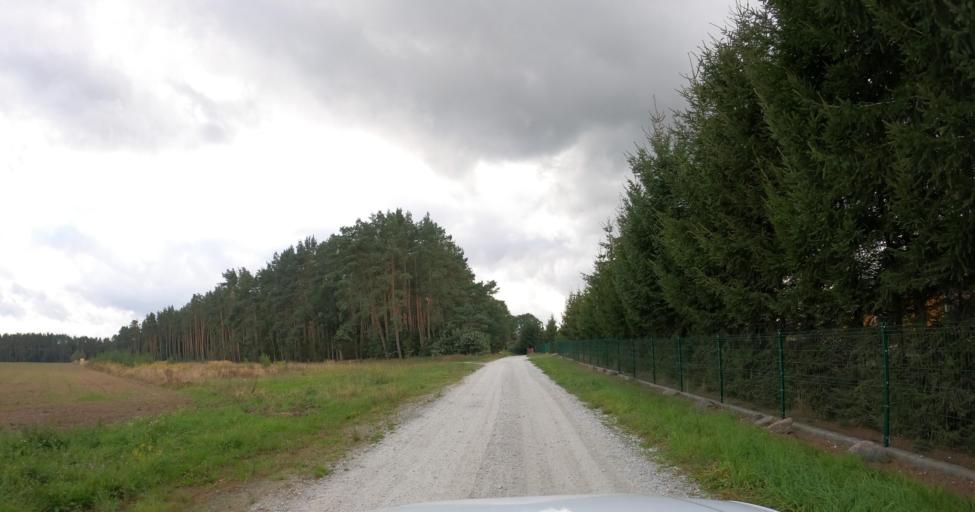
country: PL
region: West Pomeranian Voivodeship
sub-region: Powiat kolobrzeski
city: Goscino
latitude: 54.0669
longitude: 15.5848
